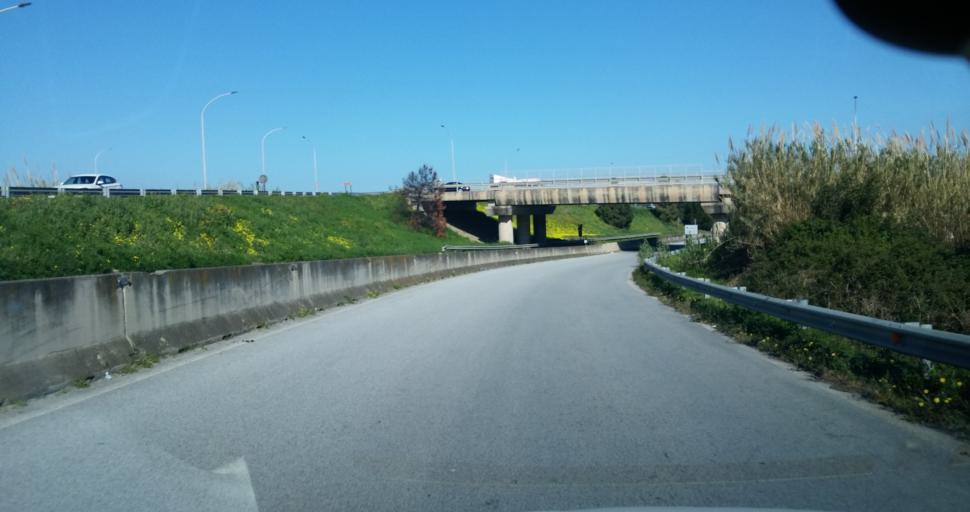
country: IT
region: Sicily
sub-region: Messina
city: Milazzo
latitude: 38.2066
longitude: 15.2387
